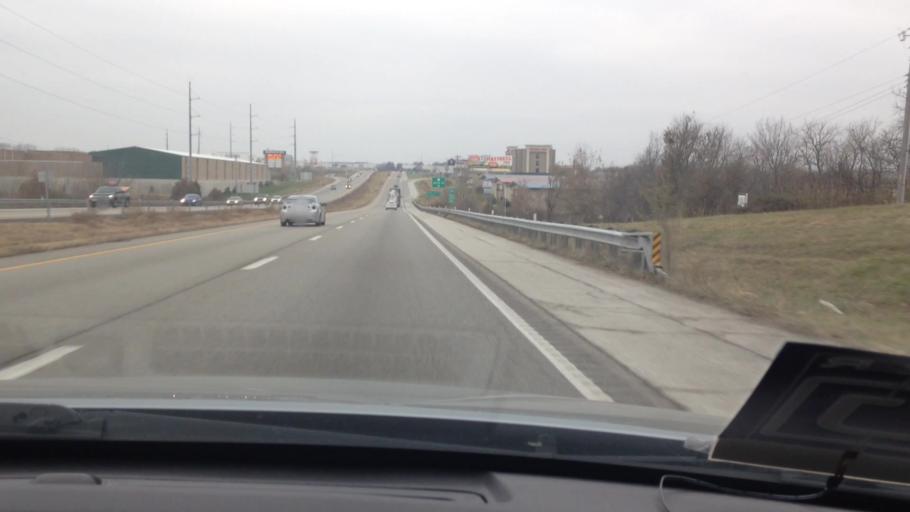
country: US
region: Missouri
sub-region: Cass County
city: Belton
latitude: 38.8205
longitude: -94.5136
